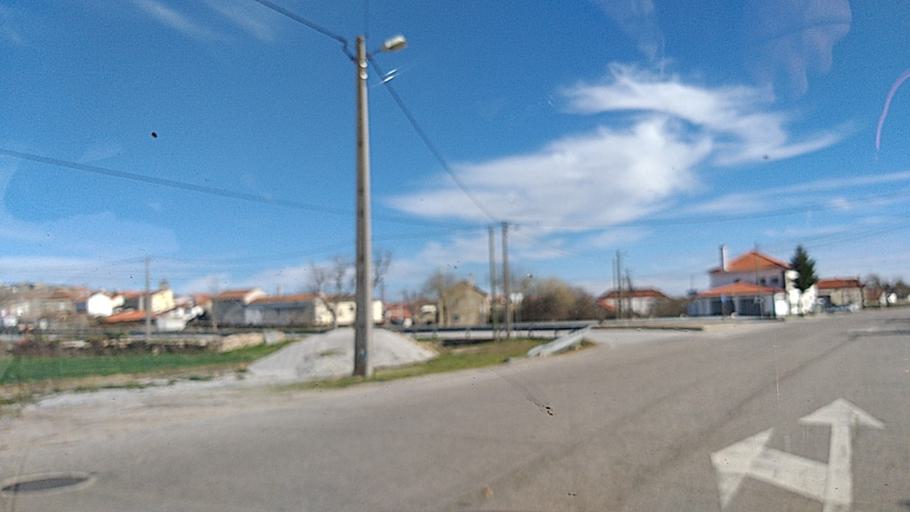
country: PT
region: Guarda
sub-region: Guarda
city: Sequeira
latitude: 40.6023
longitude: -7.0700
